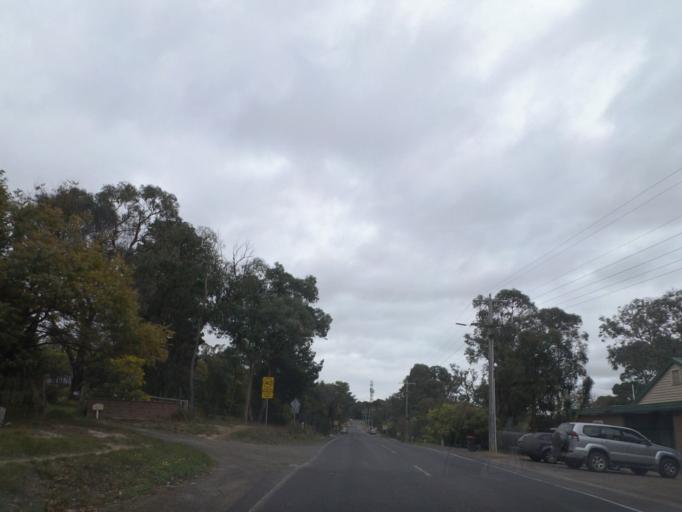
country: AU
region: Victoria
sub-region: Nillumbik
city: Diamond Creek
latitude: -37.6399
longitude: 145.1366
